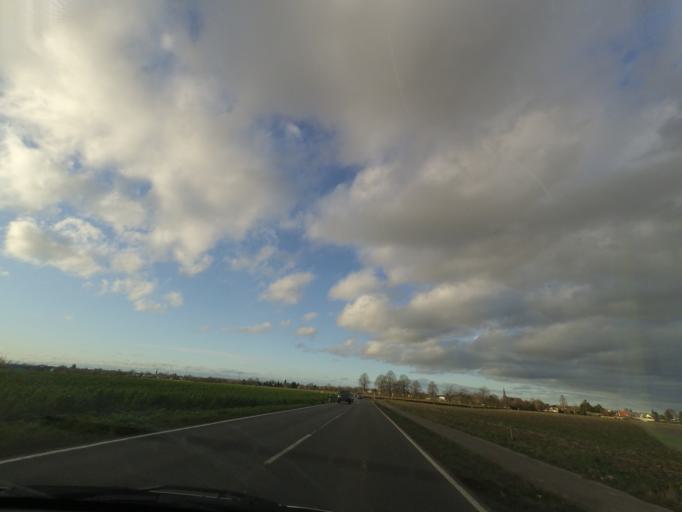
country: DE
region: North Rhine-Westphalia
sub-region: Regierungsbezirk Dusseldorf
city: Grevenbroich
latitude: 51.1113
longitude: 6.5683
